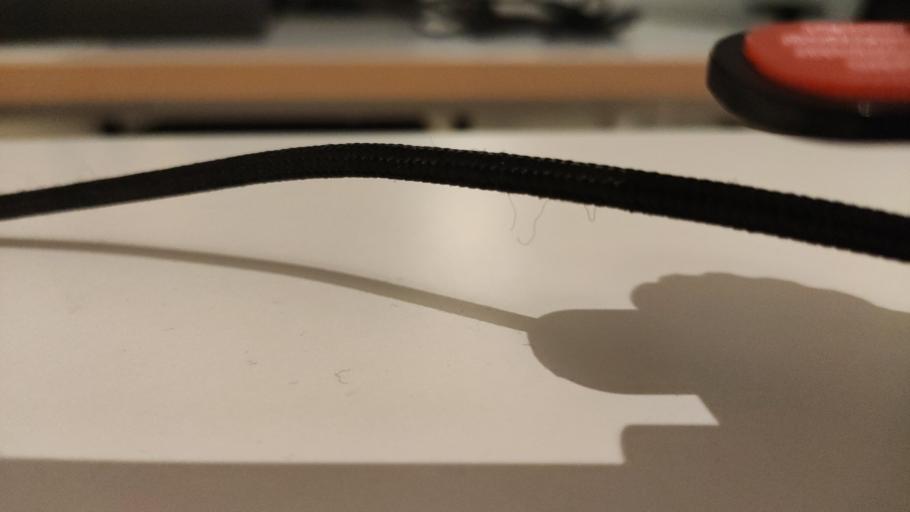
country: RU
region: Moskovskaya
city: Kurovskoye
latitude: 55.5922
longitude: 38.9229
